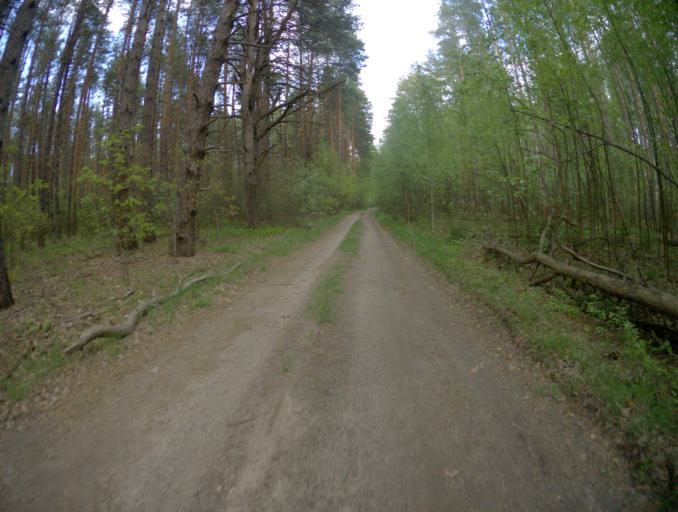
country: RU
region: Rjazan
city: Spas-Klepiki
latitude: 55.2526
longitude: 40.0993
